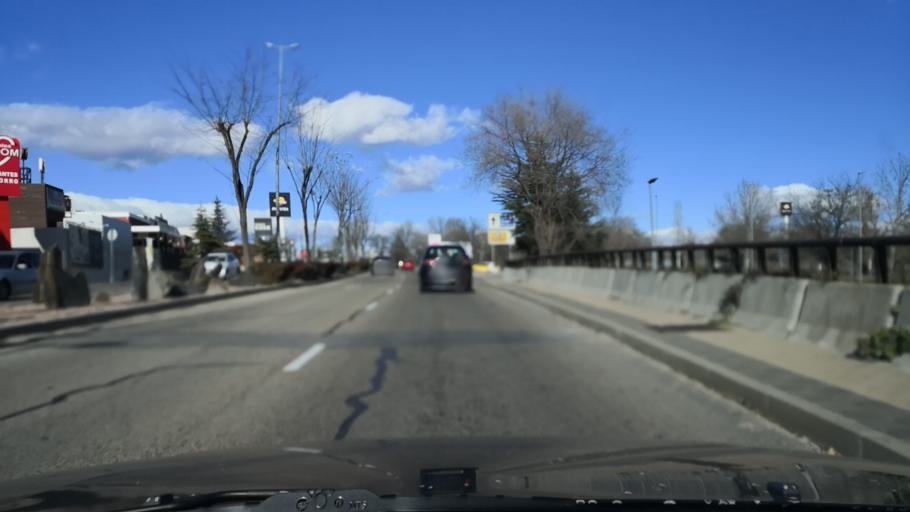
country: ES
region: Madrid
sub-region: Provincia de Madrid
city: San Sebastian de los Reyes
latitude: 40.5422
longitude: -3.6099
